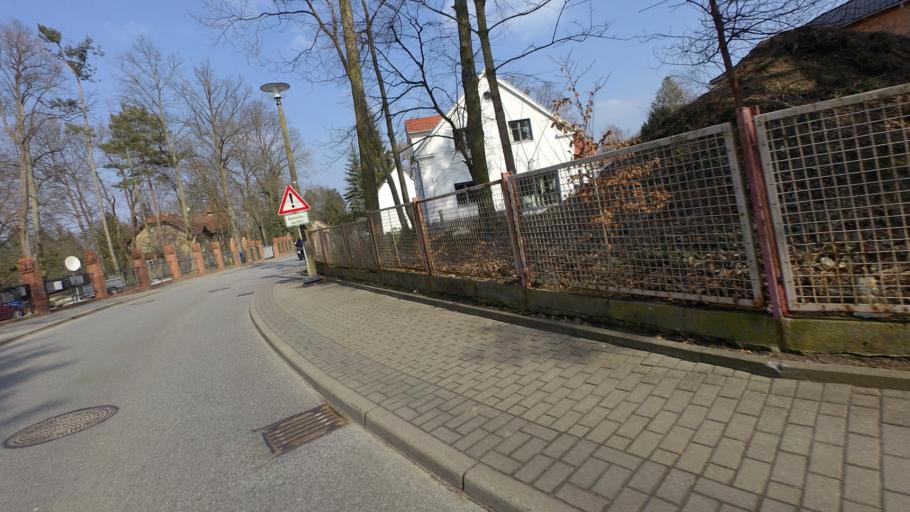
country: DE
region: Brandenburg
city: Werder
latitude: 52.3387
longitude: 12.9741
